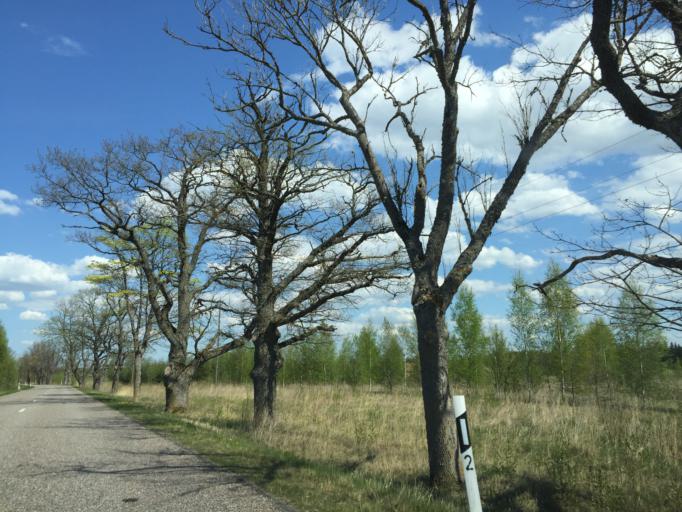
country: LV
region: Saulkrastu
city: Saulkrasti
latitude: 57.3596
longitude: 24.4860
